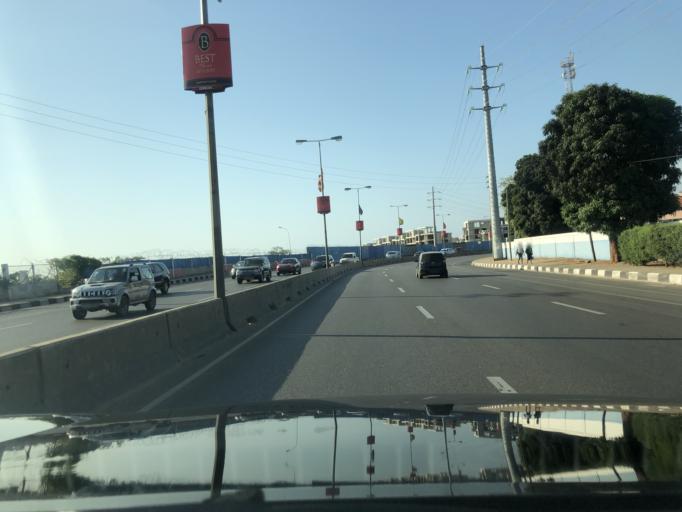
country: AO
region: Luanda
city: Luanda
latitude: -8.9000
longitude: 13.1768
